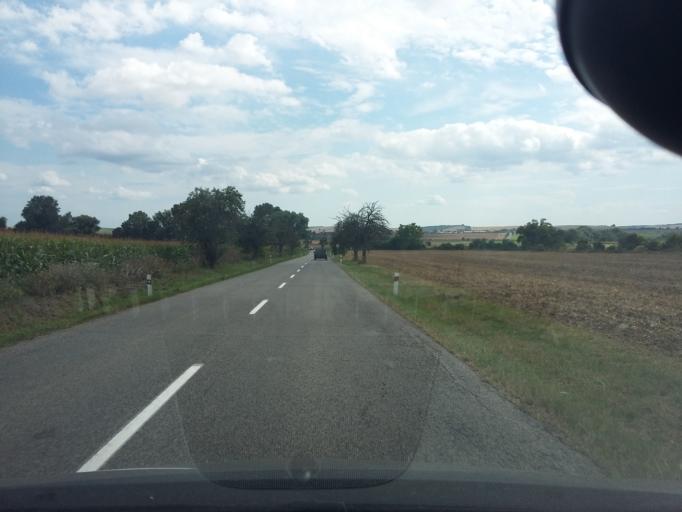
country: SK
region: Trnavsky
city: Gbely
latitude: 48.7465
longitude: 17.1706
